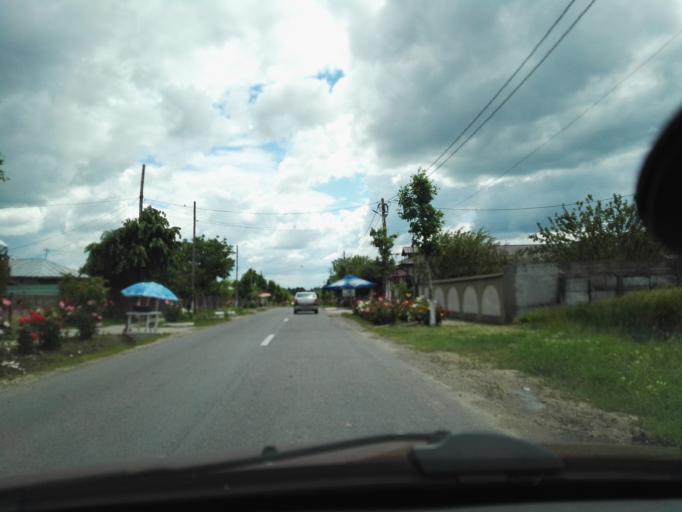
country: RO
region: Giurgiu
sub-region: Comuna Comana
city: Gradistea
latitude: 44.2255
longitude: 26.1426
